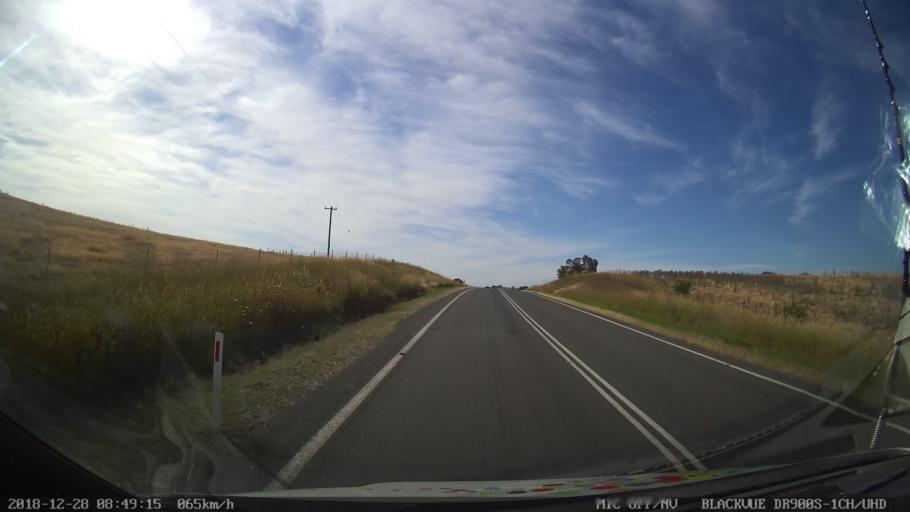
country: AU
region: New South Wales
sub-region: Upper Lachlan Shire
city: Crookwell
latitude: -34.0437
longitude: 149.3364
